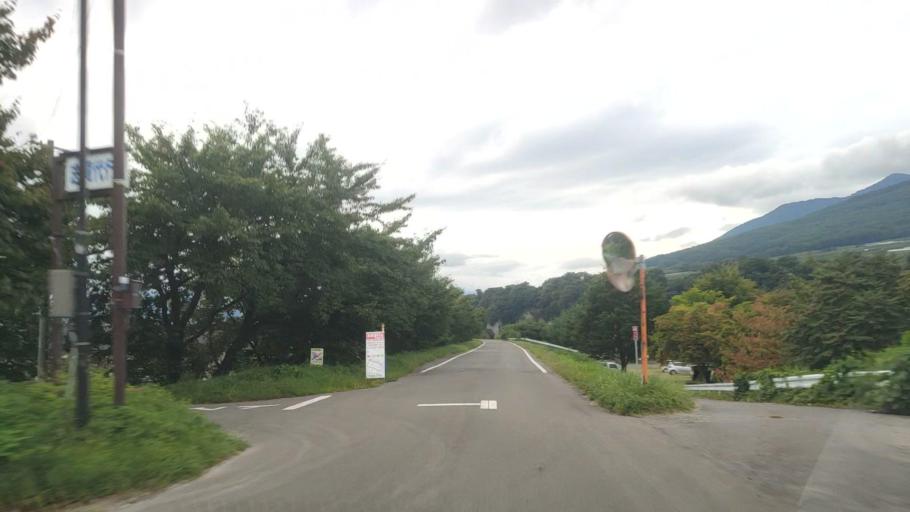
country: JP
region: Nagano
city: Nakano
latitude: 36.7662
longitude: 138.3931
